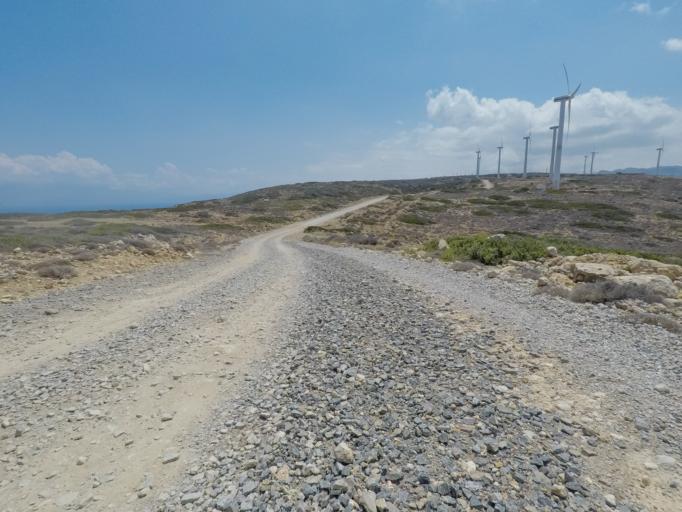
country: GR
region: Crete
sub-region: Nomos Lasithiou
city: Elounda
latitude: 35.3306
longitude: 25.7596
